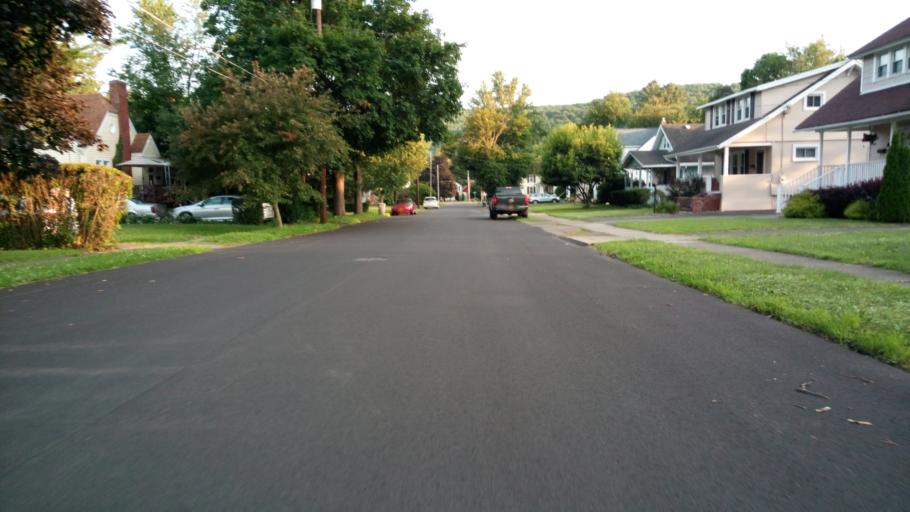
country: US
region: New York
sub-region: Chemung County
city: West Elmira
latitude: 42.0794
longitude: -76.8512
